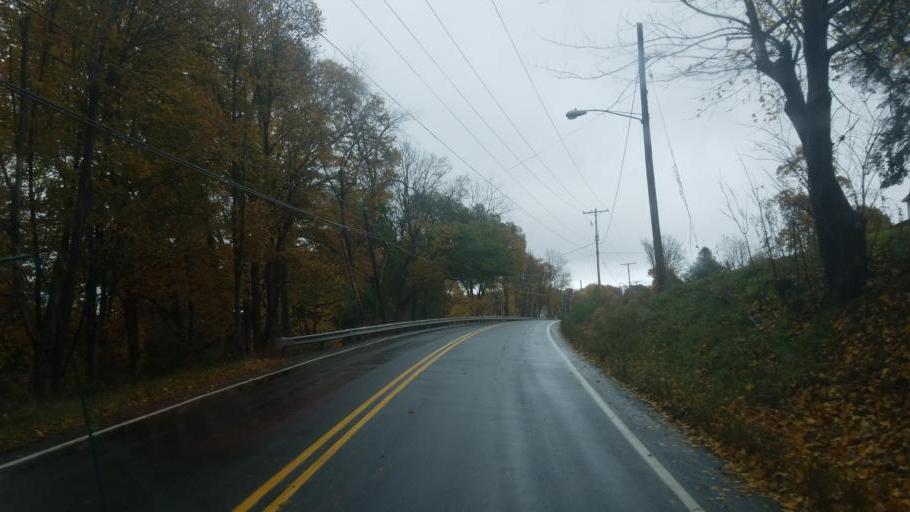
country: US
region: Pennsylvania
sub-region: Centre County
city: Milesburg
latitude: 41.0297
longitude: -77.9556
